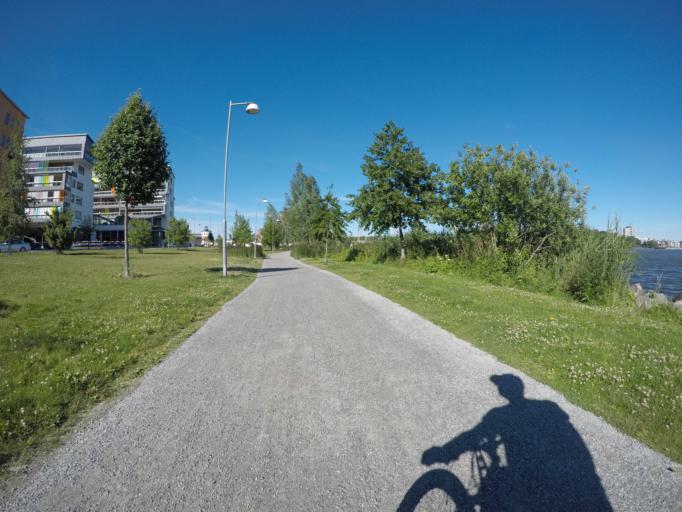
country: SE
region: Vaestmanland
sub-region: Vasteras
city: Vasteras
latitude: 59.6035
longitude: 16.5615
